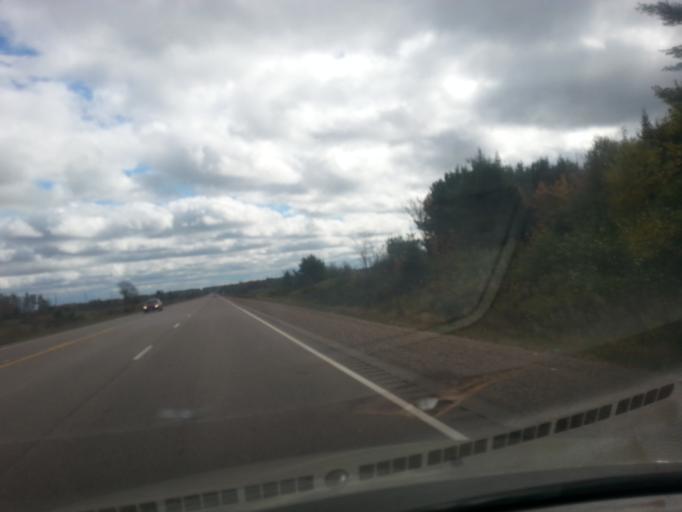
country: CA
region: Ontario
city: Petawawa
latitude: 45.8326
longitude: -77.2348
